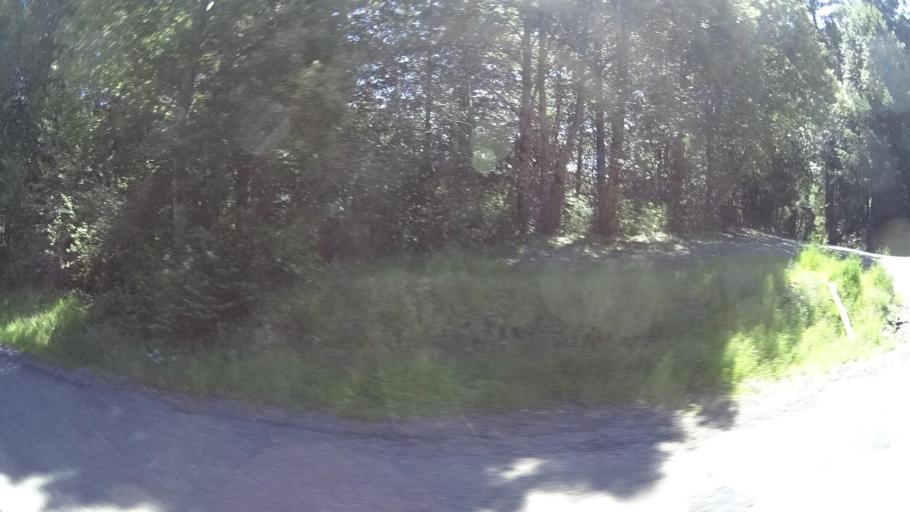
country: US
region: California
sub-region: Humboldt County
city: Redway
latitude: 40.1779
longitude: -124.0890
